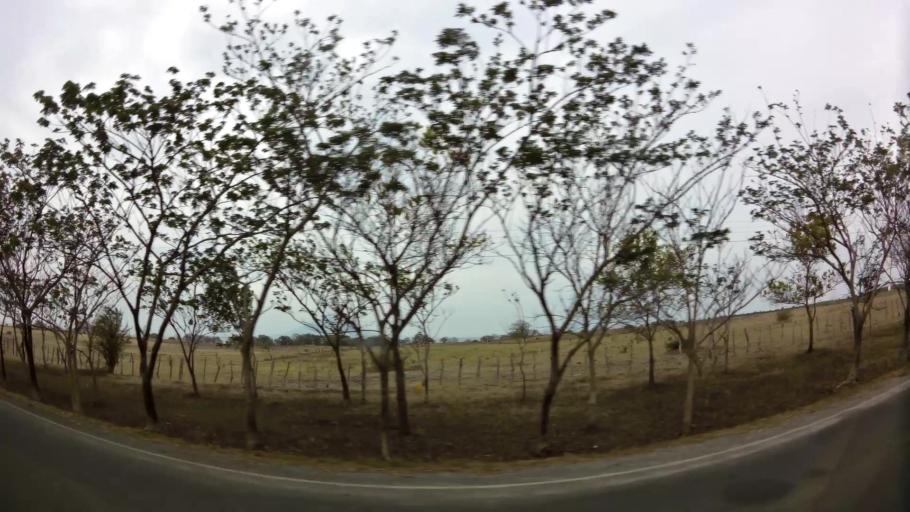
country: NI
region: Rivas
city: San Jorge
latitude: 11.3266
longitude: -85.7174
